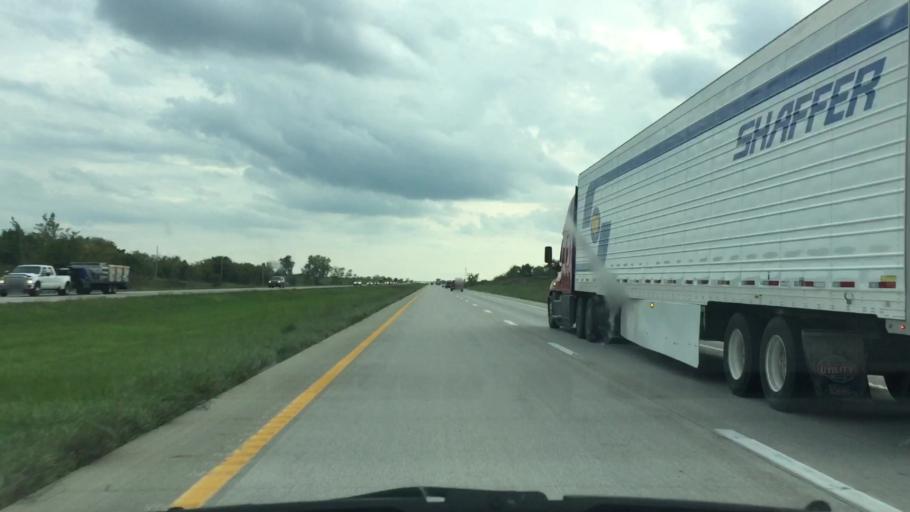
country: US
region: Missouri
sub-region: Clinton County
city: Lathrop
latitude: 39.6018
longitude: -94.2533
